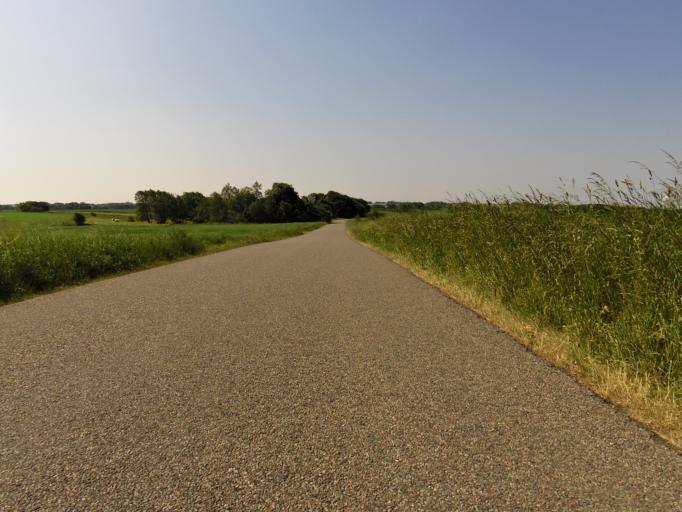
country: DK
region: Central Jutland
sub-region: Holstebro Kommune
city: Vinderup
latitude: 56.4801
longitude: 8.8293
